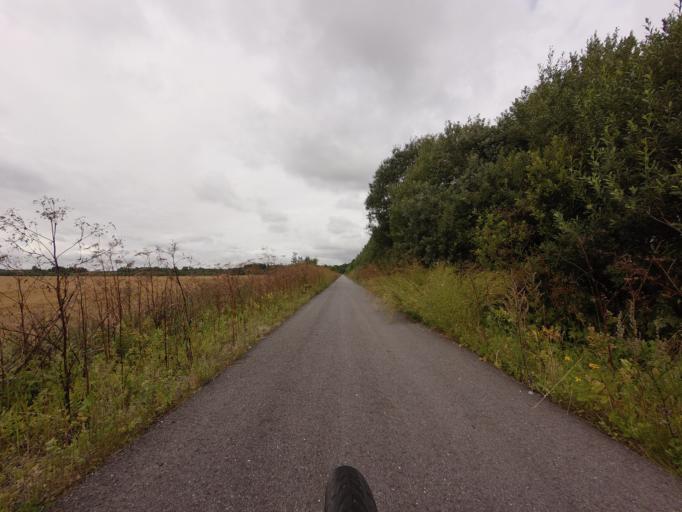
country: DK
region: Central Jutland
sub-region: Syddjurs Kommune
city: Ryomgard
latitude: 56.3847
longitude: 10.4625
